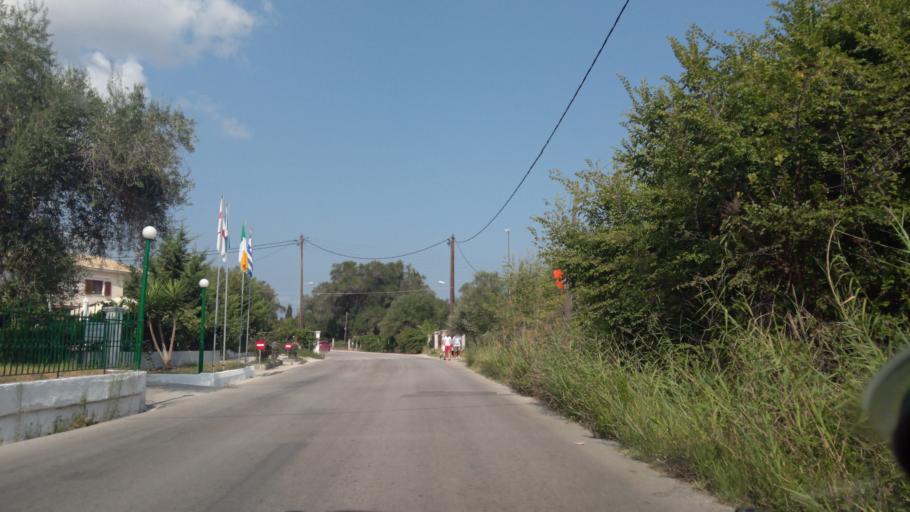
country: GR
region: Ionian Islands
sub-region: Nomos Kerkyras
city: Lefkimmi
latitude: 39.4049
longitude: 20.0965
